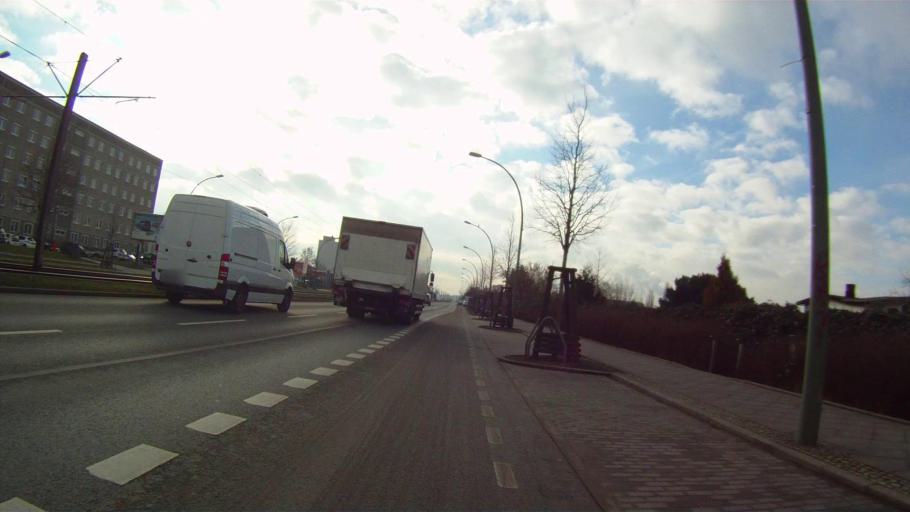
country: DE
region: Berlin
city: Friedrichsfelde
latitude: 52.5205
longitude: 13.5193
